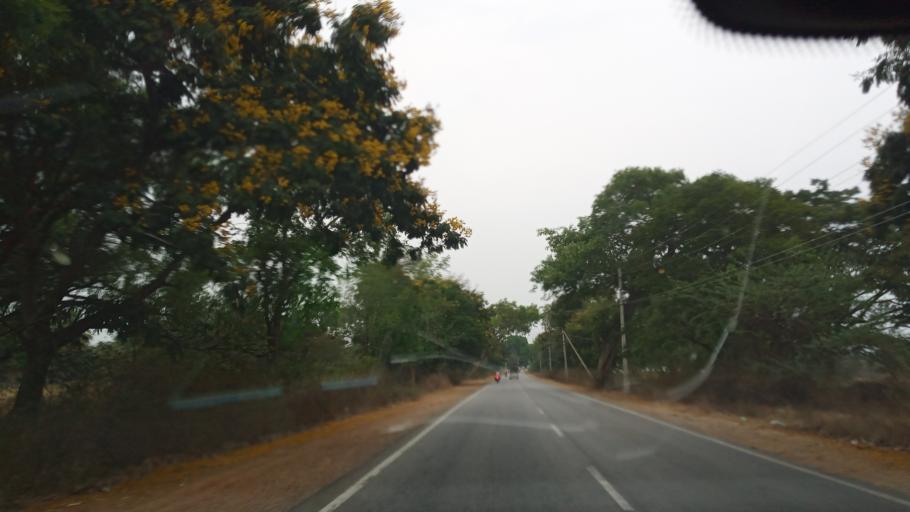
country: IN
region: Karnataka
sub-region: Mandya
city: Belluru
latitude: 12.9566
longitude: 76.7567
